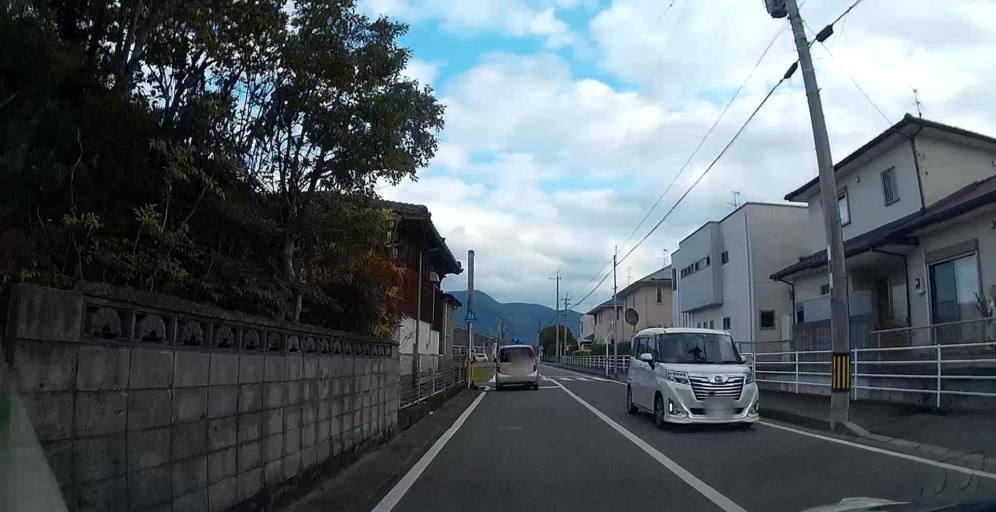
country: JP
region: Kumamoto
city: Yatsushiro
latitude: 32.5376
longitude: 130.6300
